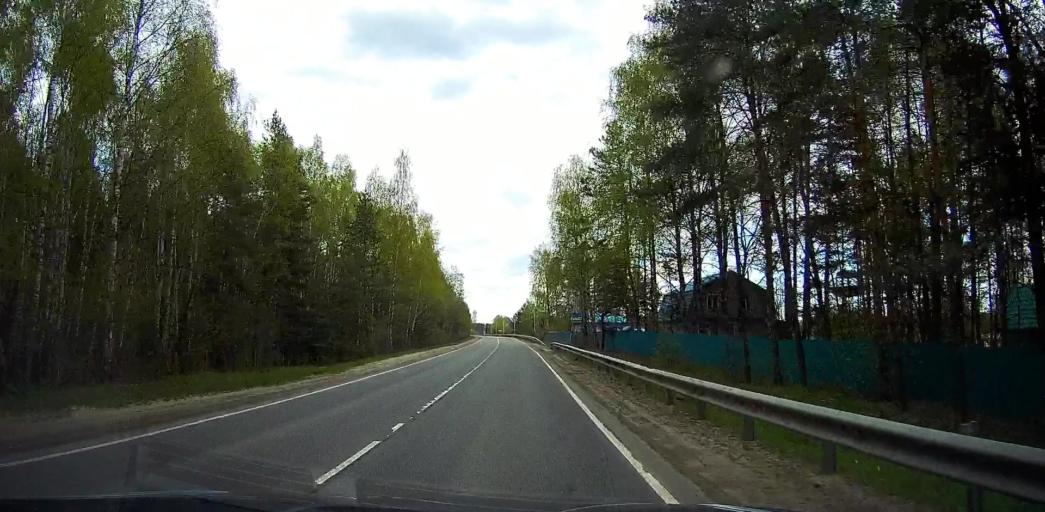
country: RU
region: Moskovskaya
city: Pavlovskiy Posad
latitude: 55.8008
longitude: 38.6577
